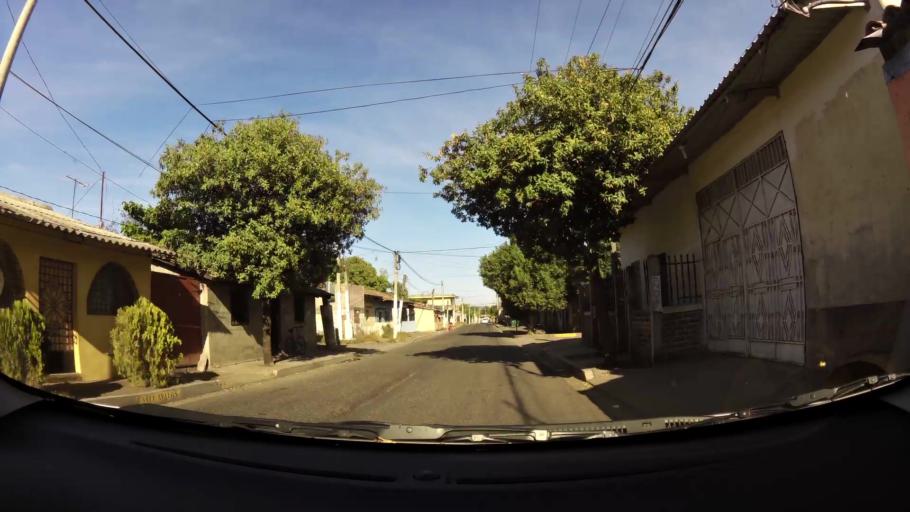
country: SV
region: San Miguel
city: San Miguel
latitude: 13.4685
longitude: -88.1922
